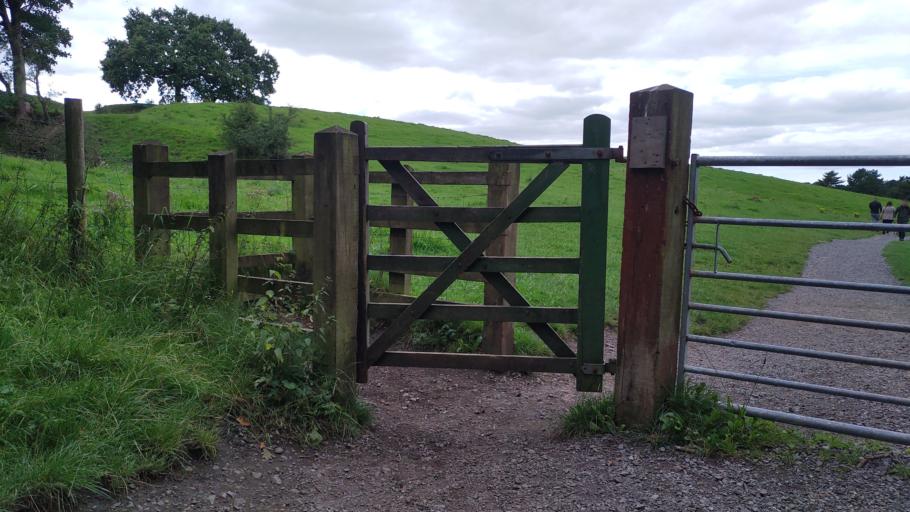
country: GB
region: England
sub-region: Lancashire
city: Clayton-le-Woods
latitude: 53.7112
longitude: -2.6493
